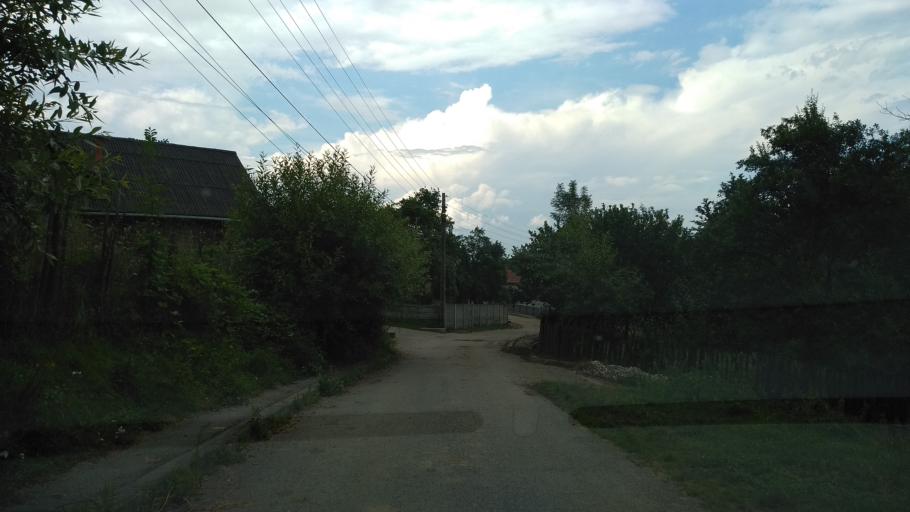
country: RO
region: Hunedoara
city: Salasu de Sus
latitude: 45.4856
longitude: 22.9462
